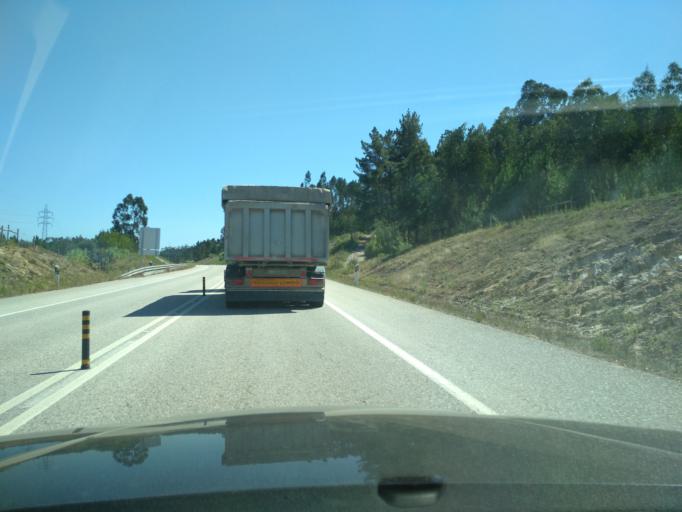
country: PT
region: Leiria
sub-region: Pombal
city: Lourical
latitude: 39.9554
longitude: -8.6906
